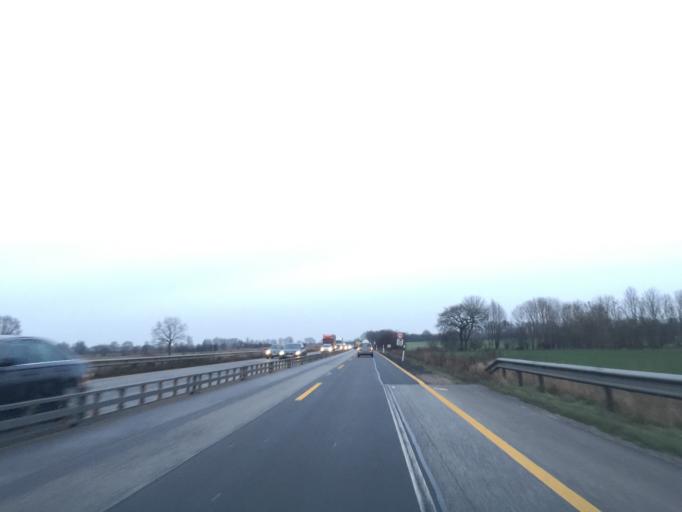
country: DE
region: Schleswig-Holstein
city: Loop
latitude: 54.1395
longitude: 9.9622
